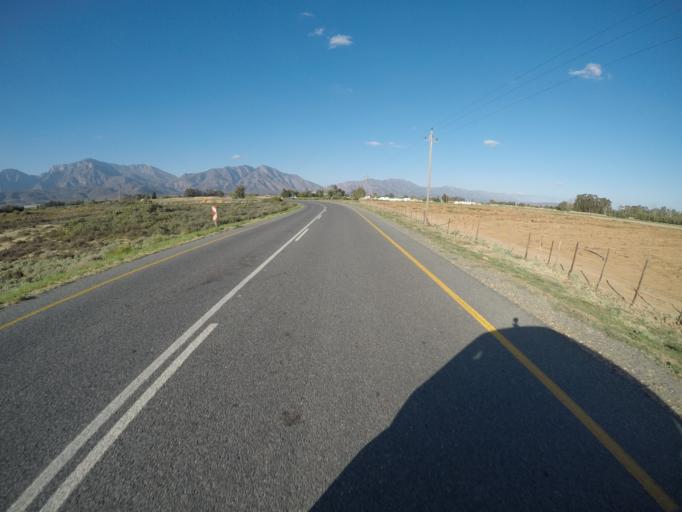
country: ZA
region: Western Cape
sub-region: Cape Winelands District Municipality
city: Worcester
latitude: -33.6720
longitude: 19.5400
